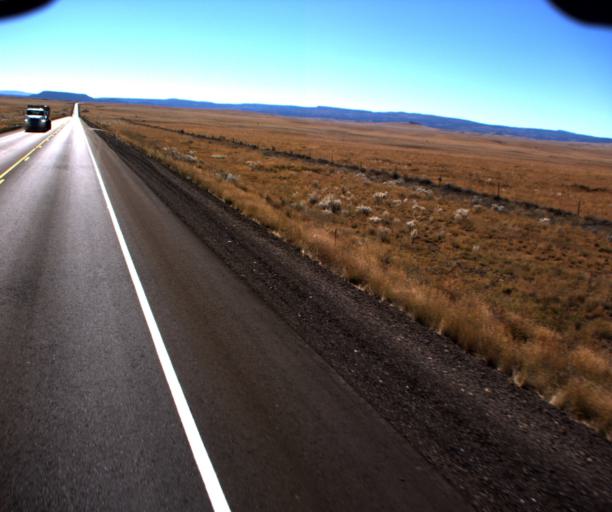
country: US
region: Arizona
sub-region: Apache County
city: Springerville
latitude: 34.2234
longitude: -109.3371
